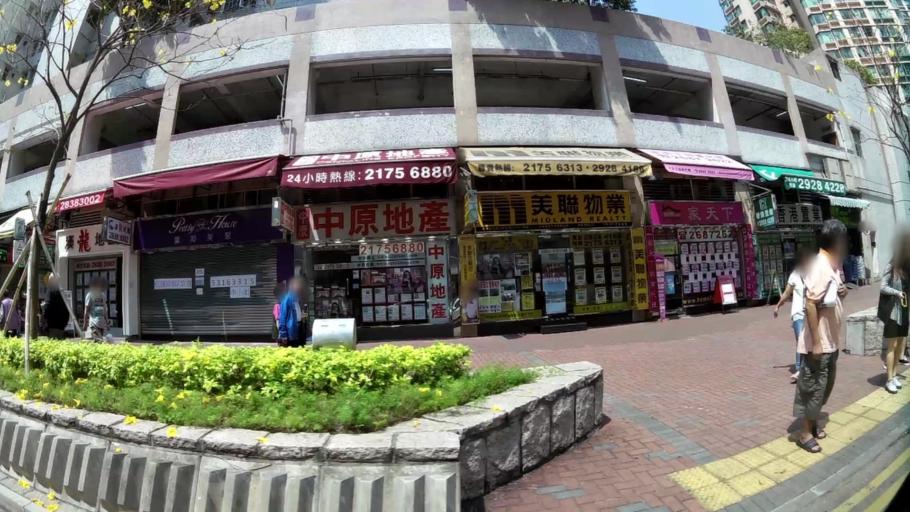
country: HK
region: Sham Shui Po
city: Sham Shui Po
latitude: 22.3150
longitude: 114.1640
